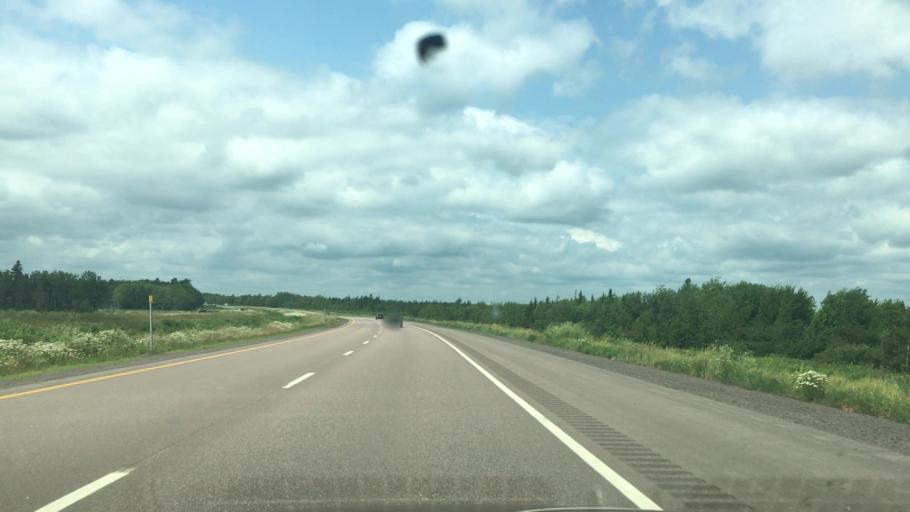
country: CA
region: New Brunswick
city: Dieppe
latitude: 46.1245
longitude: -64.6363
